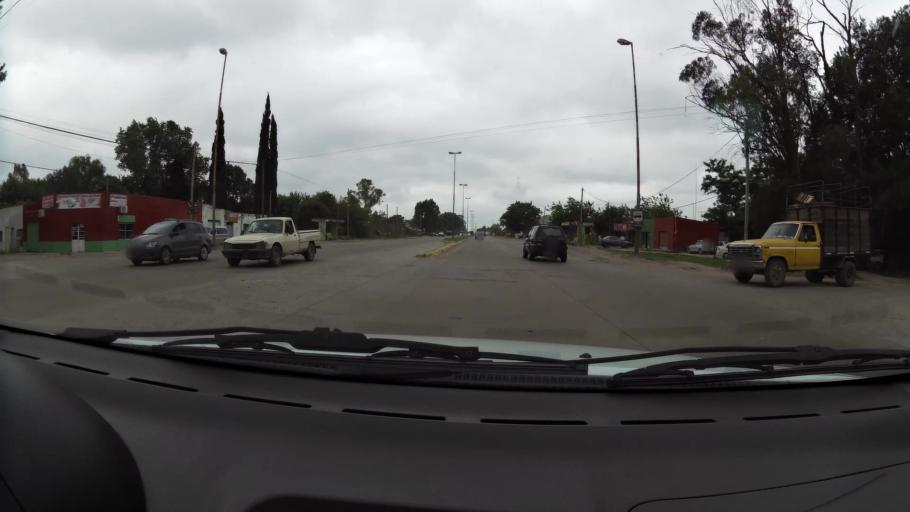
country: AR
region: Buenos Aires
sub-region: Partido de La Plata
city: La Plata
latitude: -35.0156
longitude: -58.0703
